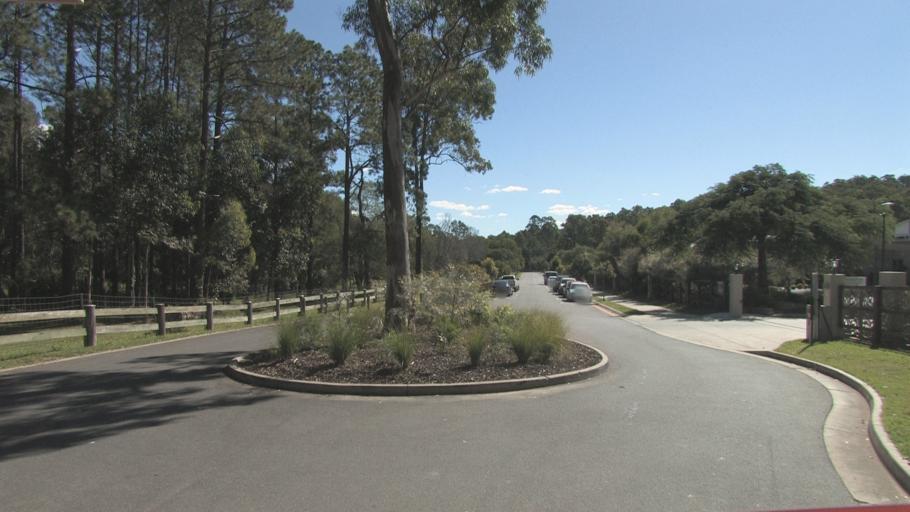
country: AU
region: Queensland
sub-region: Logan
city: Springwood
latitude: -27.6187
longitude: 153.1511
